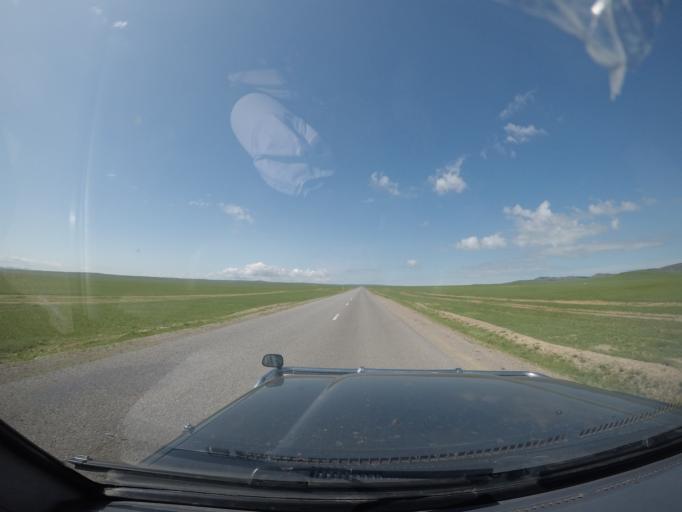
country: MN
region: Hentiy
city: Bayan
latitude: 47.3219
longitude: 111.4190
